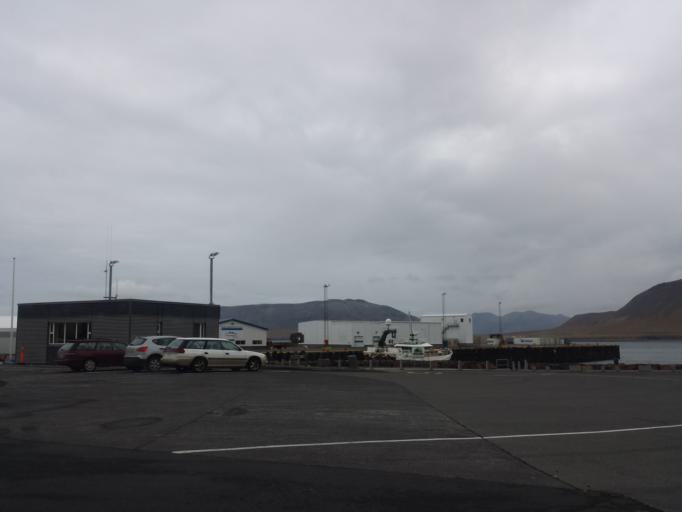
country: IS
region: West
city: Olafsvik
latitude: 64.9252
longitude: -23.2558
